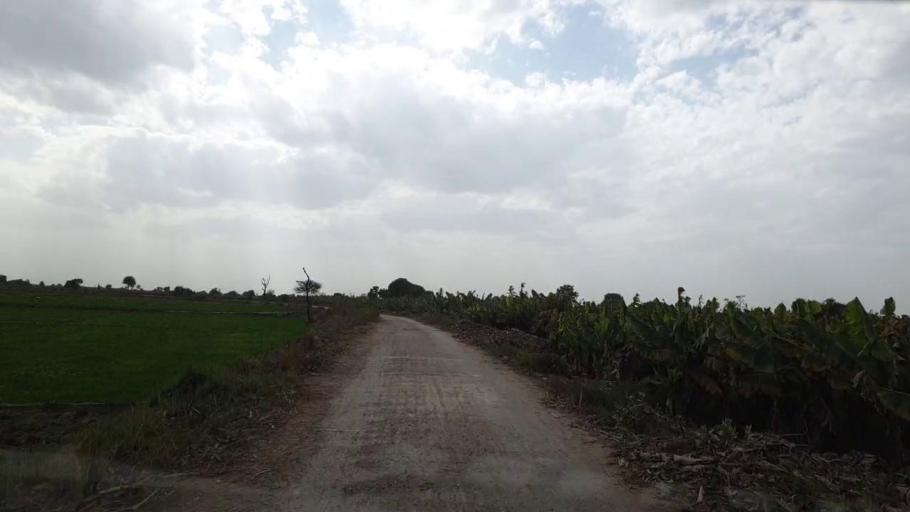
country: PK
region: Sindh
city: Tando Jam
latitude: 25.5517
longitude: 68.5752
